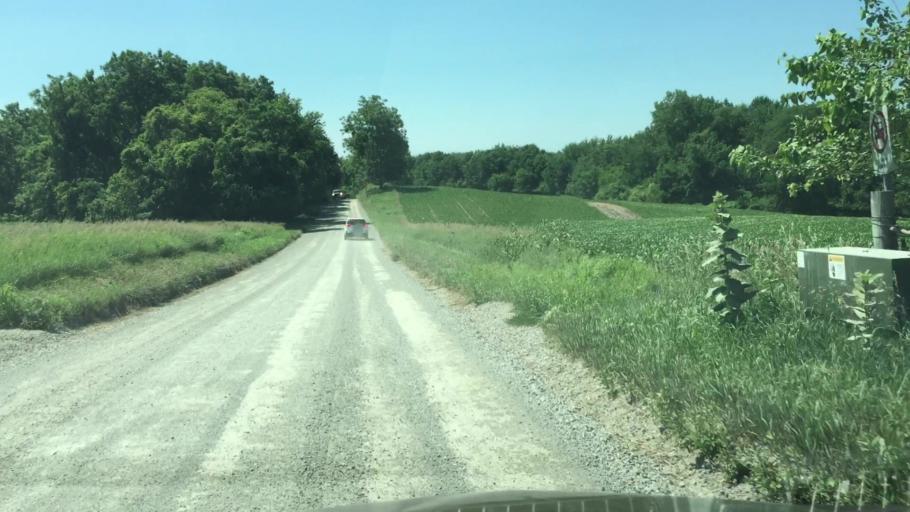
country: US
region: Iowa
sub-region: Linn County
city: Ely
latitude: 41.8220
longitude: -91.5896
